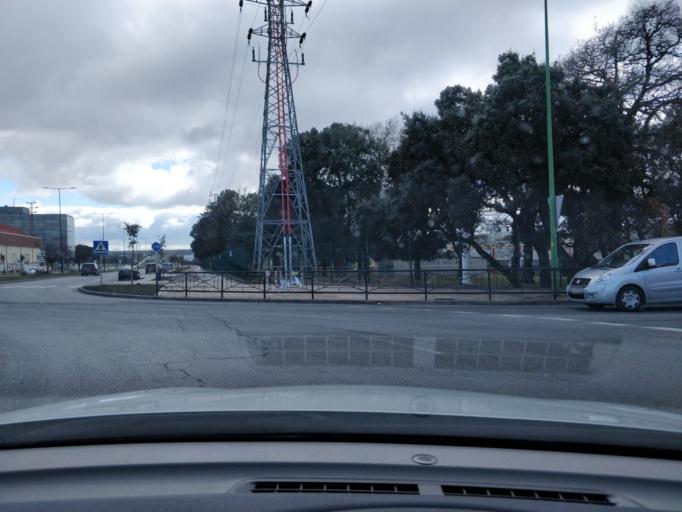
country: ES
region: Castille and Leon
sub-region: Provincia de Burgos
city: Burgos
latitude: 42.3584
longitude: -3.6515
